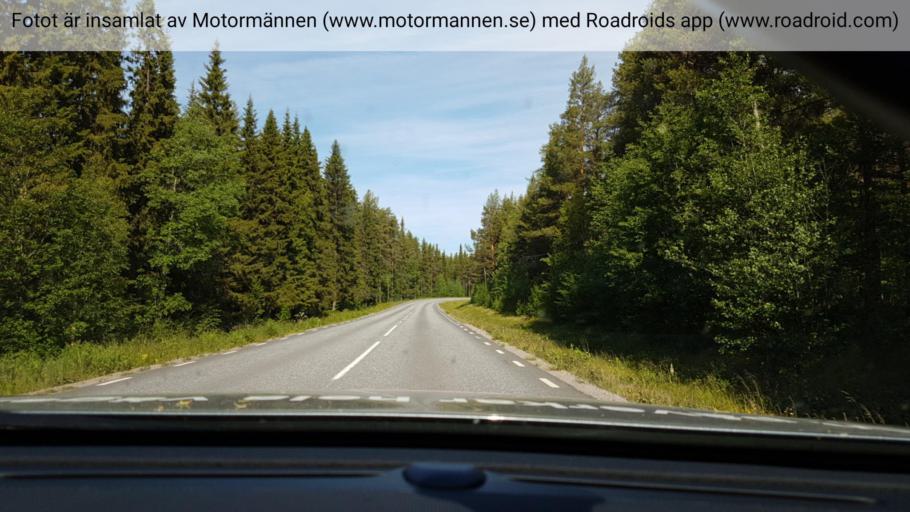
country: SE
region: Vaesterbotten
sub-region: Dorotea Kommun
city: Dorotea
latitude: 64.2671
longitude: 16.3512
